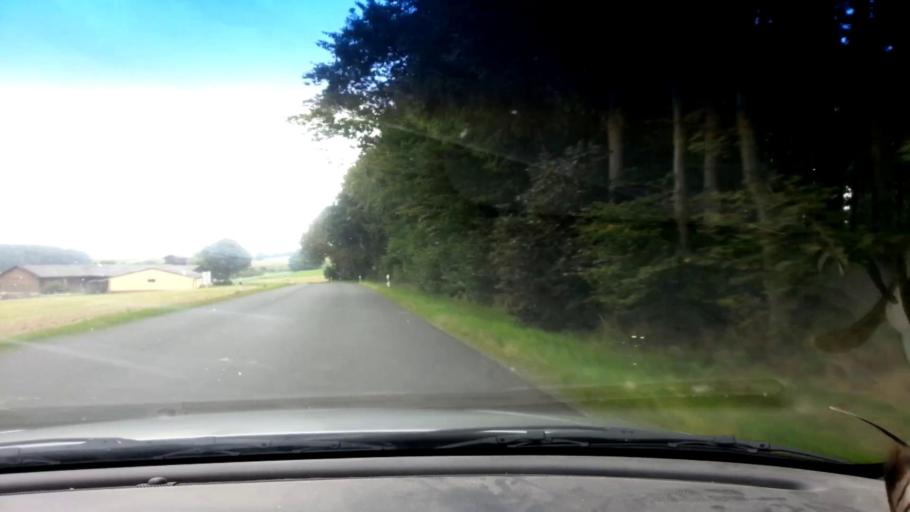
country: DE
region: Bavaria
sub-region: Upper Palatinate
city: Waldsassen
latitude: 50.0242
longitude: 12.2619
